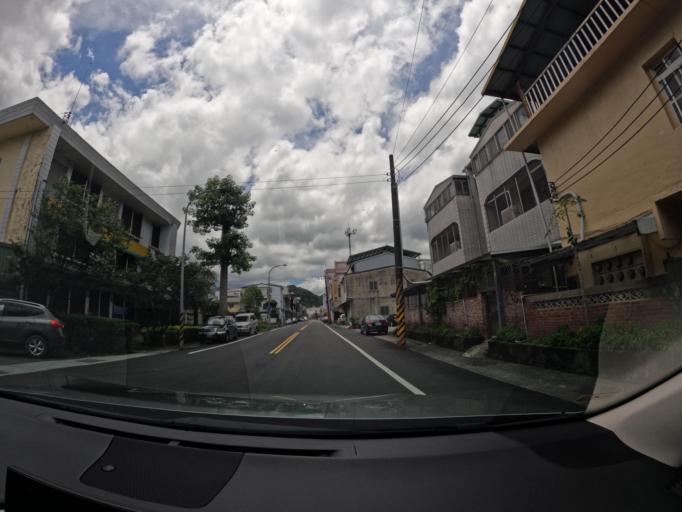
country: TW
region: Taiwan
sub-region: Miaoli
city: Miaoli
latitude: 24.6035
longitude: 121.0005
